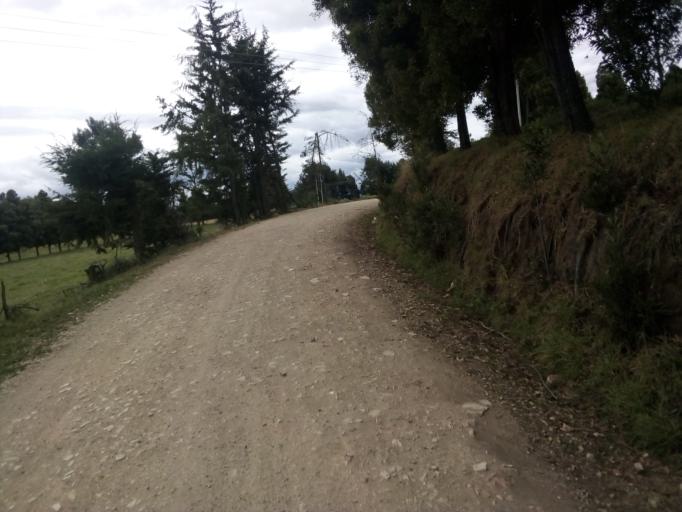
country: CO
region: Boyaca
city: Toca
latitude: 5.5820
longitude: -73.1442
